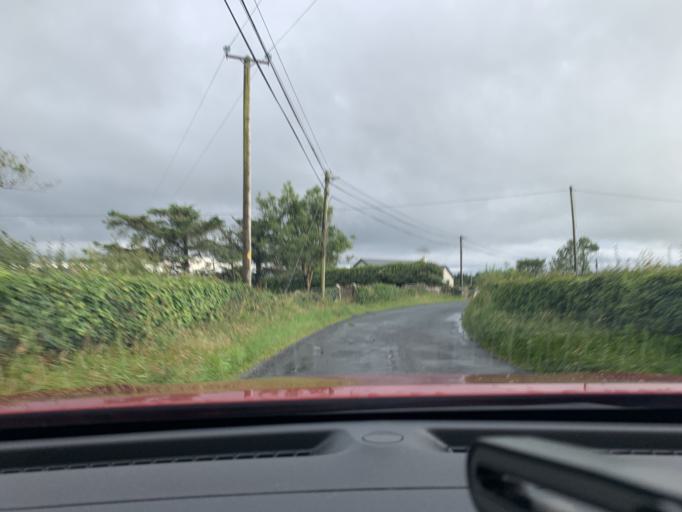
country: IE
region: Connaught
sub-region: Sligo
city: Strandhill
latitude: 54.3579
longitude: -8.5421
